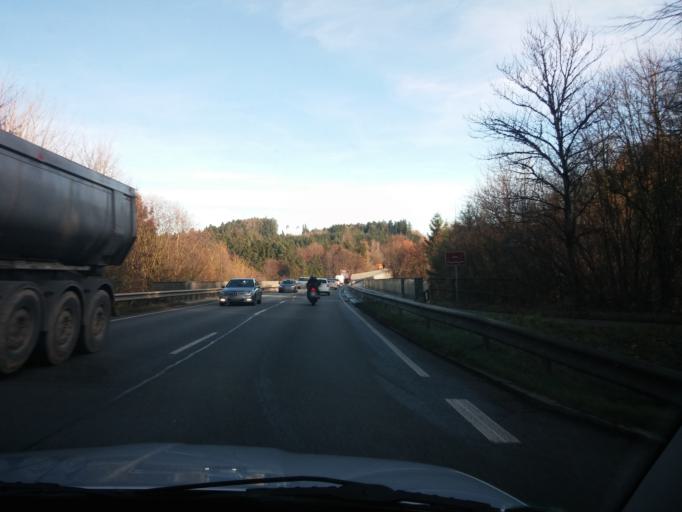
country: DE
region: Bavaria
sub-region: Upper Bavaria
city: Wasserburg am Inn
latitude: 48.0681
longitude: 12.2124
